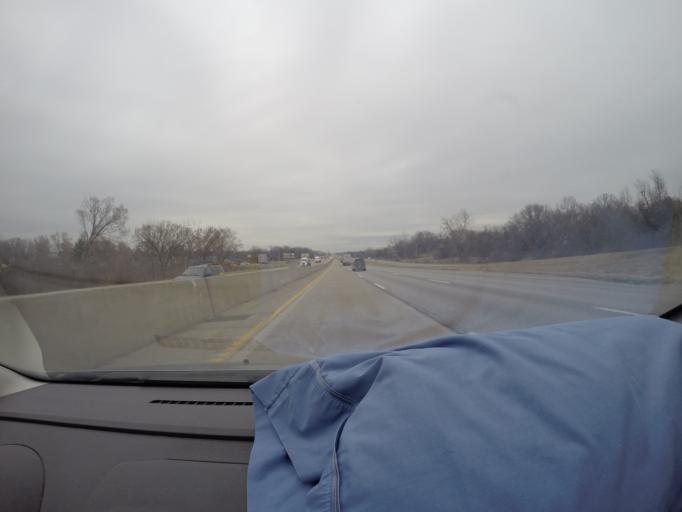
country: US
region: Missouri
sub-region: Saint Charles County
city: Lake Saint Louis
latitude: 38.8053
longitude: -90.8028
